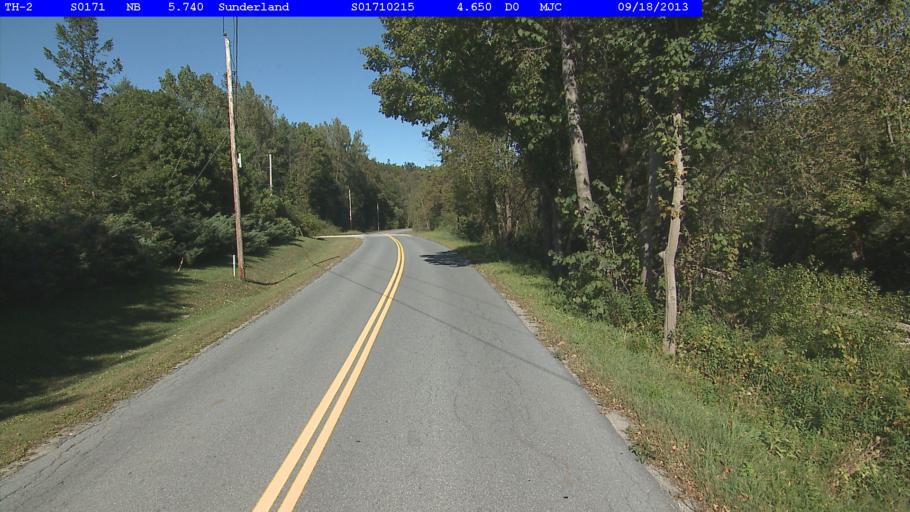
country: US
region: Vermont
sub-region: Bennington County
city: Manchester Center
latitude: 43.1174
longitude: -73.0927
